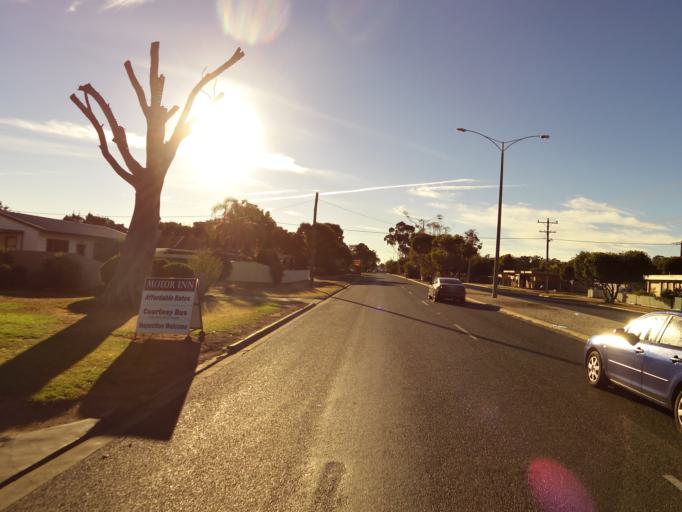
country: AU
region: Victoria
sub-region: Campaspe
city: Echuca
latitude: -36.1404
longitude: 144.7354
